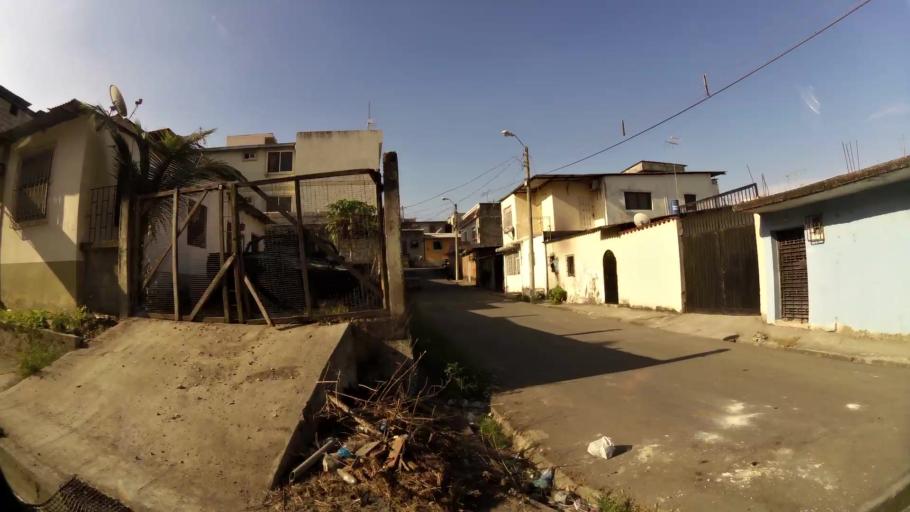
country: EC
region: Guayas
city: Guayaquil
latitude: -2.1565
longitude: -79.9143
